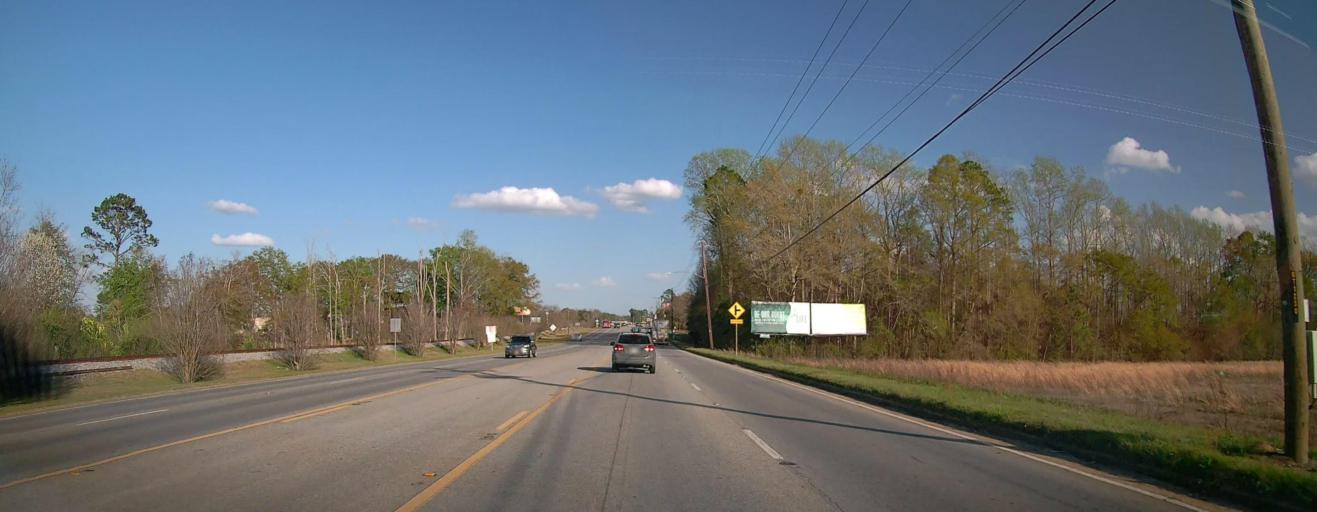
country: US
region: Georgia
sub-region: Toombs County
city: Lyons
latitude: 32.2035
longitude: -82.3525
